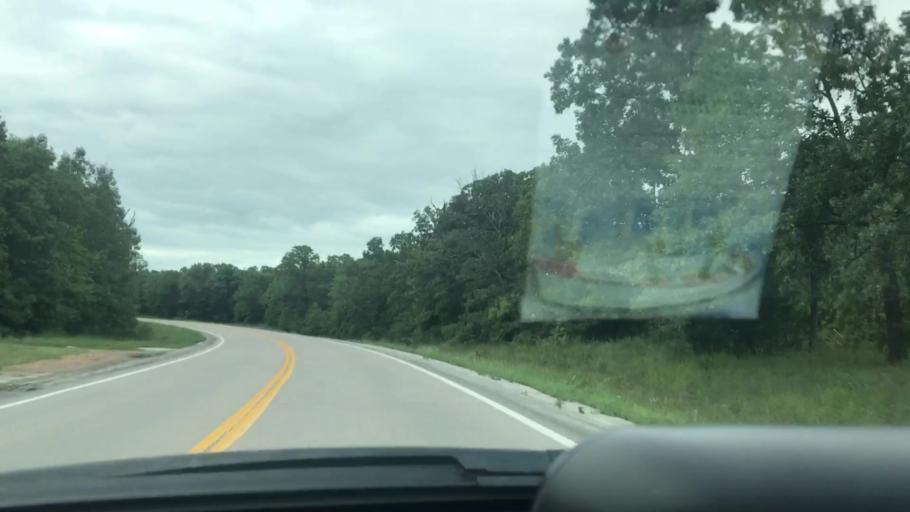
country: US
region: Missouri
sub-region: Benton County
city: Warsaw
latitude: 38.1591
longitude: -93.2975
